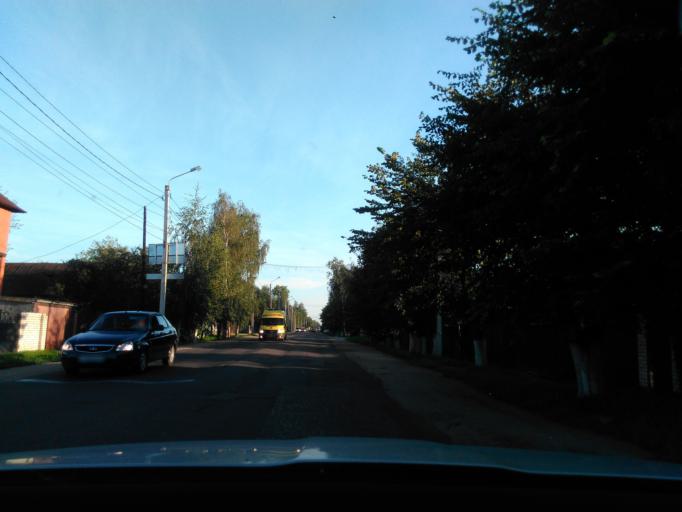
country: RU
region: Tverskaya
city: Konakovo
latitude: 56.7021
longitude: 36.7680
